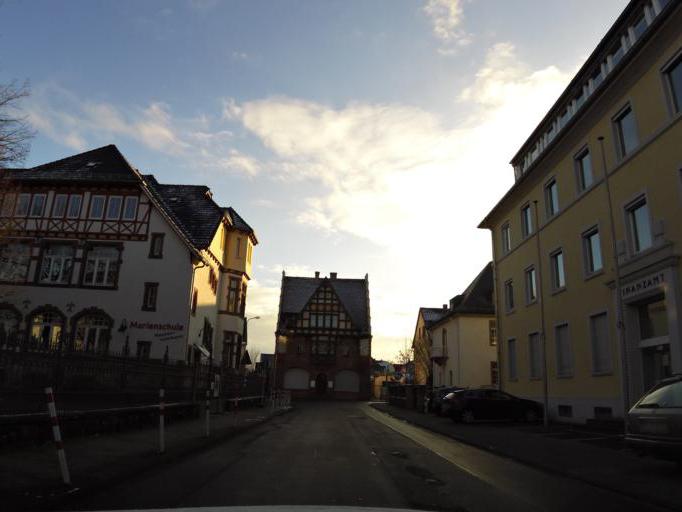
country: DE
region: Hesse
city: Dieburg
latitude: 49.8998
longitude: 8.8431
